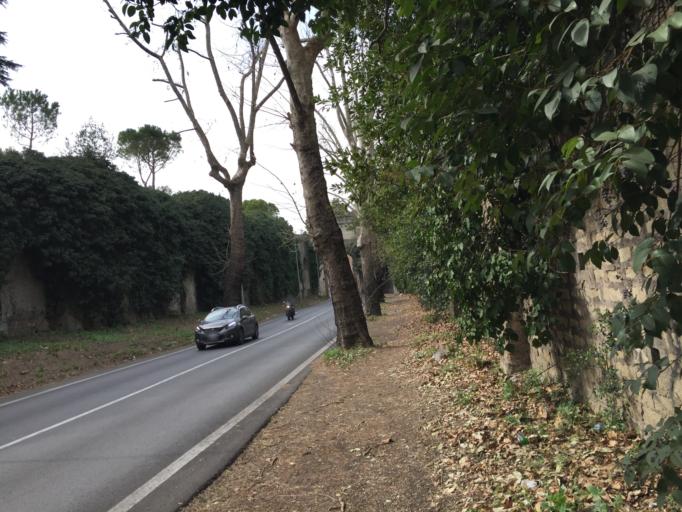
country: VA
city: Vatican City
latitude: 41.8888
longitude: 12.4543
